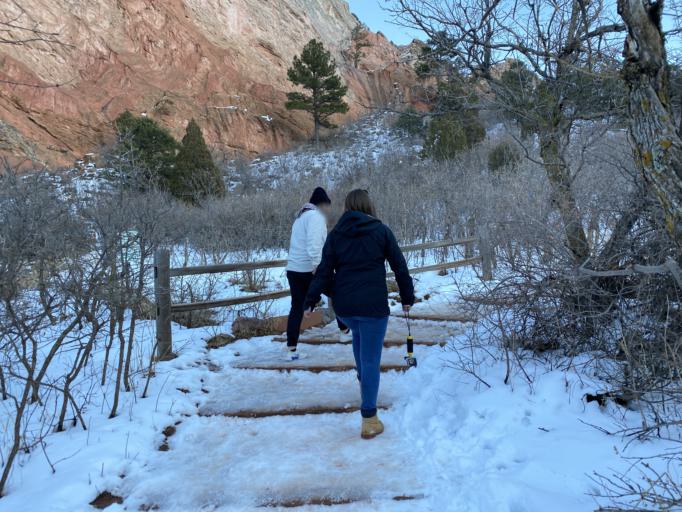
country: US
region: Colorado
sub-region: El Paso County
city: Manitou Springs
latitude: 38.8756
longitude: -104.8807
